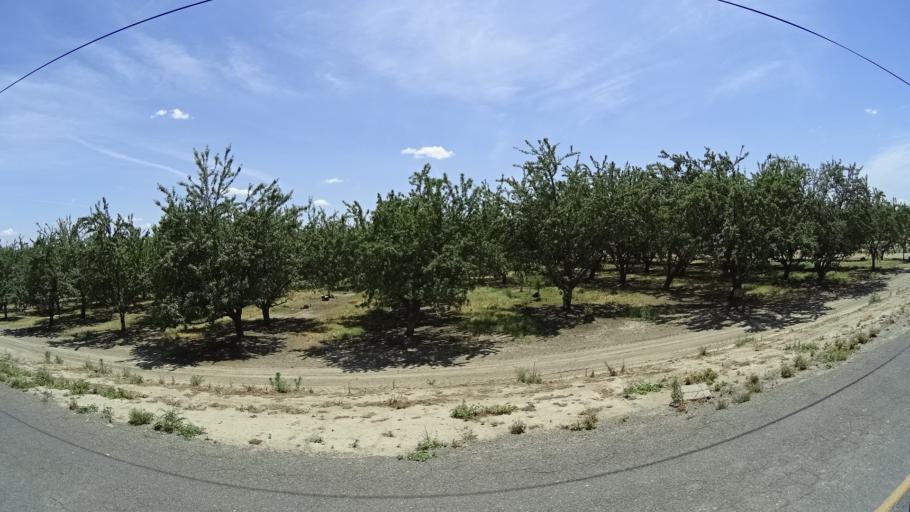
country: US
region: California
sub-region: Kings County
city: Armona
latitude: 36.2839
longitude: -119.7032
